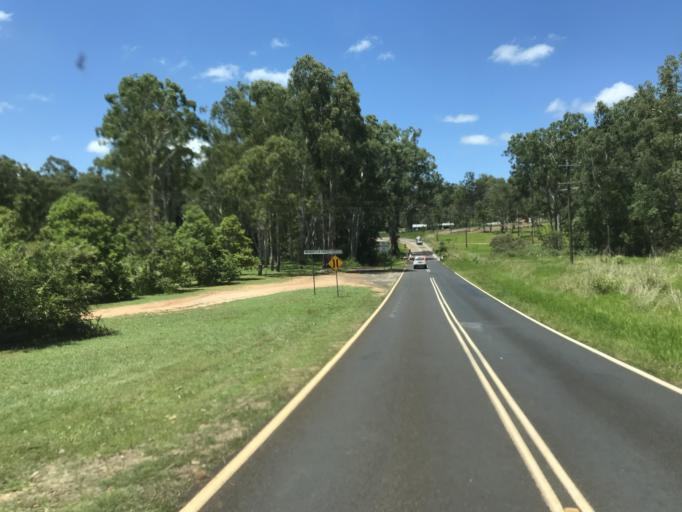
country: AU
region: Queensland
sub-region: Tablelands
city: Atherton
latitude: -17.4142
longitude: 145.3928
